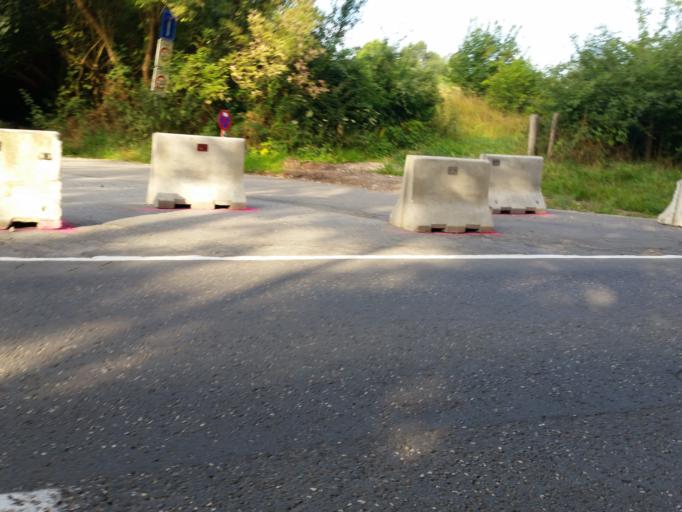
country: BE
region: Flanders
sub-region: Provincie Vlaams-Brabant
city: Vilvoorde
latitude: 50.9366
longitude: 4.4071
